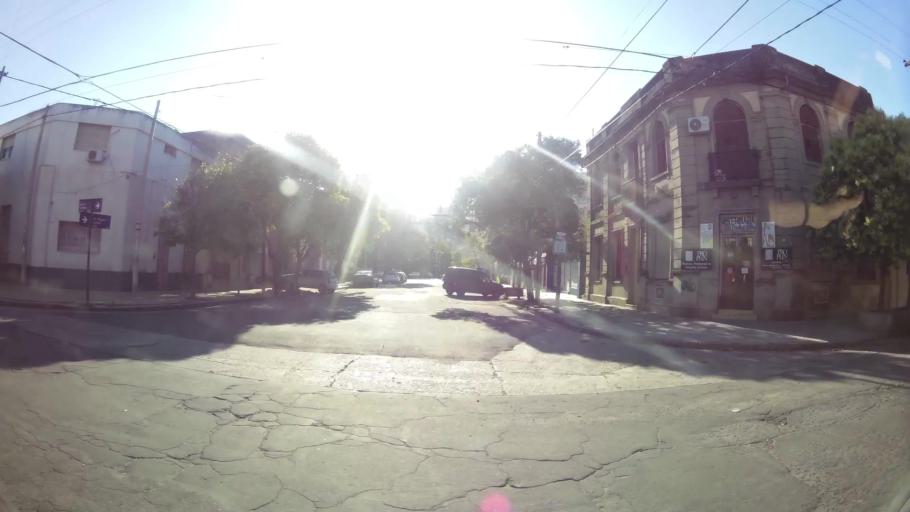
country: AR
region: Cordoba
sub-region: Departamento de Capital
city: Cordoba
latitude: -31.3910
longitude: -64.1825
